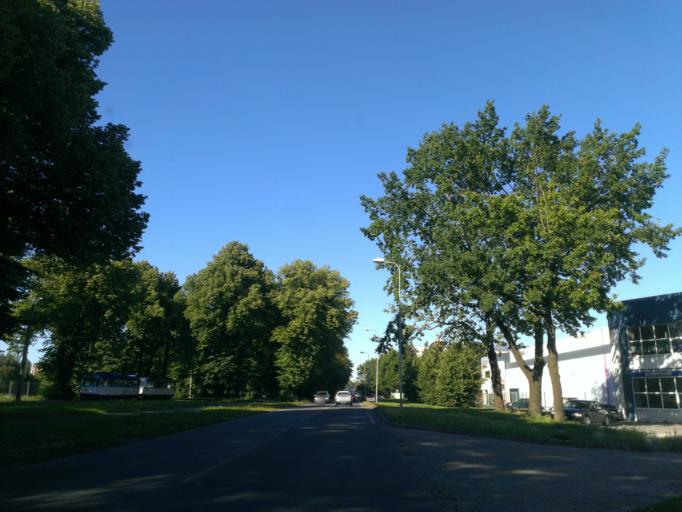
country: LV
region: Riga
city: Jaunciems
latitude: 56.9870
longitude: 24.1620
